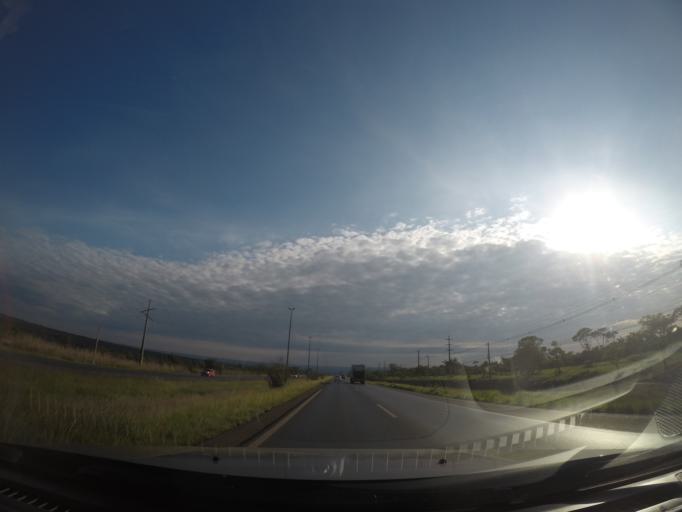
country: BR
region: Goias
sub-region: Planaltina
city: Planaltina
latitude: -15.6330
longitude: -47.7381
